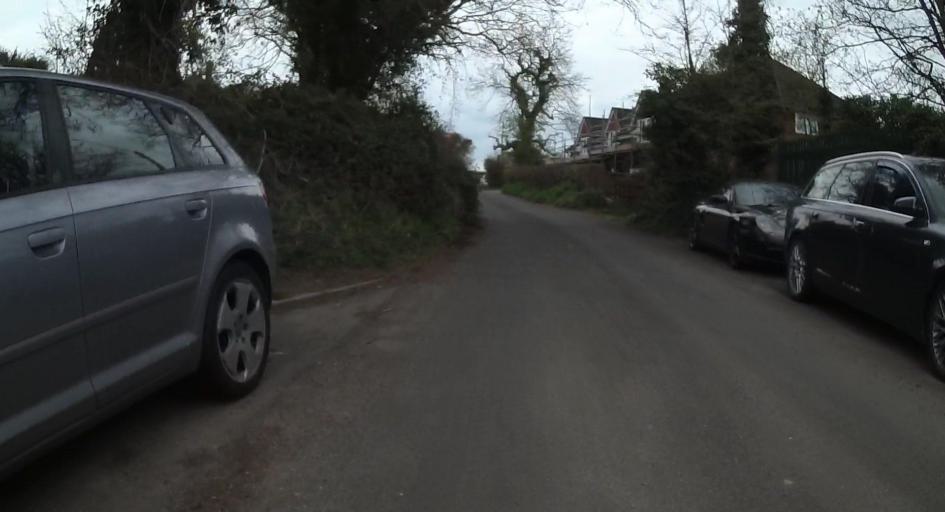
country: GB
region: England
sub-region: Hampshire
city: Long Sutton
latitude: 51.2233
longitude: -0.9673
